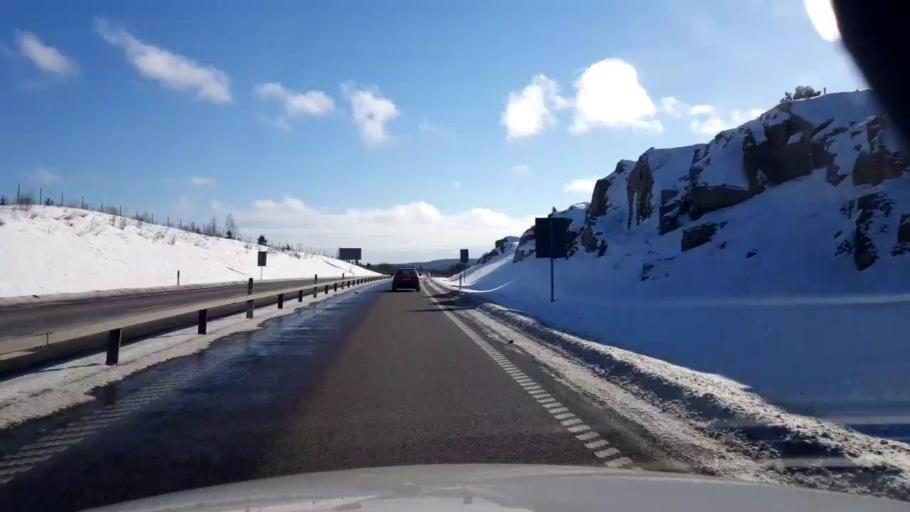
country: SE
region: Vaesternorrland
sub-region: Sundsvalls Kommun
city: Njurundabommen
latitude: 62.2595
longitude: 17.3652
